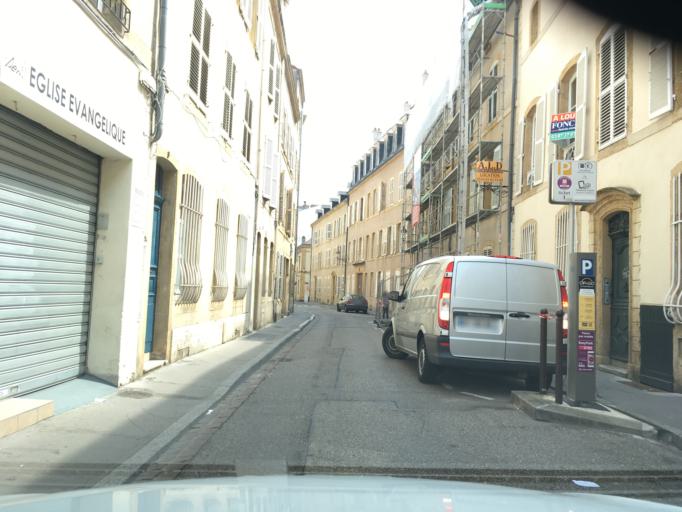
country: FR
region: Lorraine
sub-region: Departement de la Moselle
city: Metz
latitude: 49.1135
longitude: 6.1753
